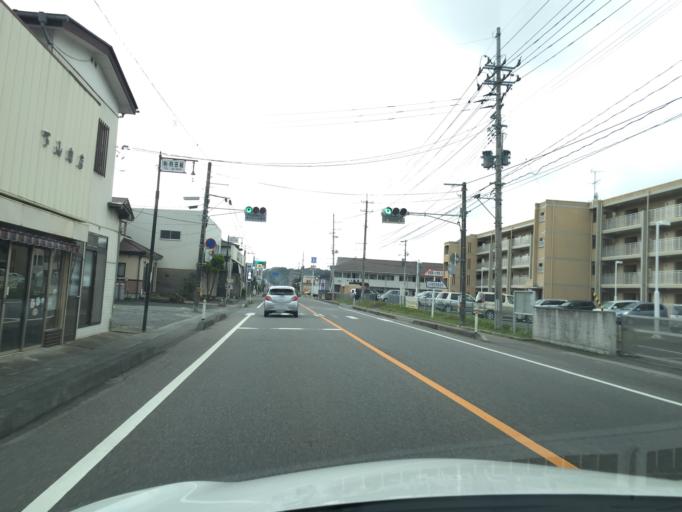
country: JP
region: Fukushima
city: Iwaki
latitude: 37.0659
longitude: 140.8513
